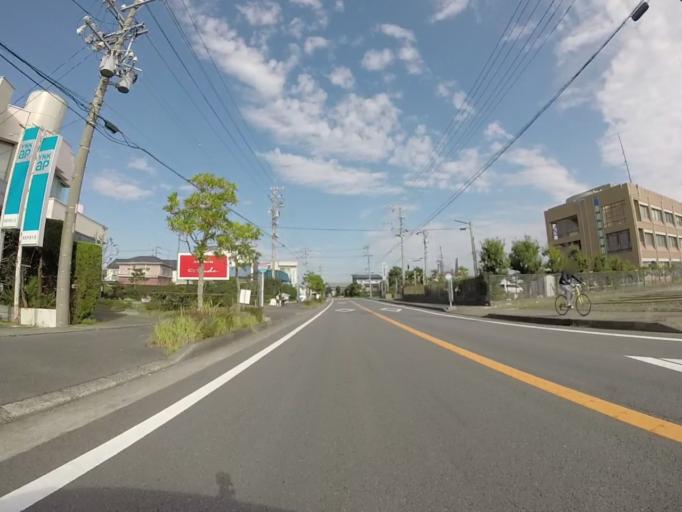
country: JP
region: Shizuoka
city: Sagara
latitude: 34.7579
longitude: 138.2420
